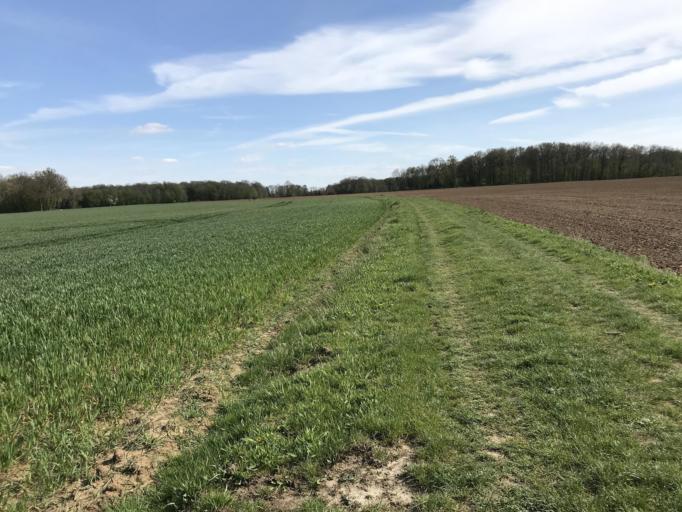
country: FR
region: Ile-de-France
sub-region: Departement de l'Essonne
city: Gometz-le-Chatel
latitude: 48.6681
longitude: 2.1530
